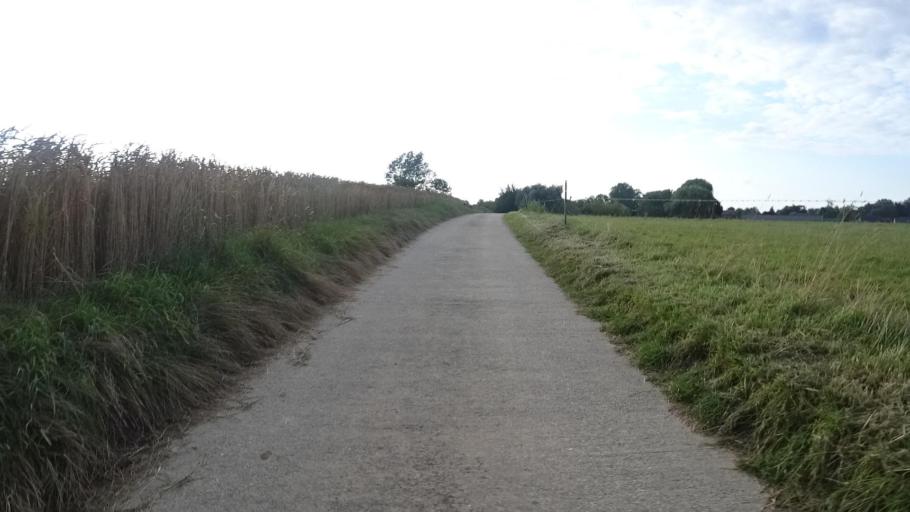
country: BE
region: Wallonia
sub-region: Province du Brabant Wallon
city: Walhain-Saint-Paul
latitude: 50.6387
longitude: 4.6833
